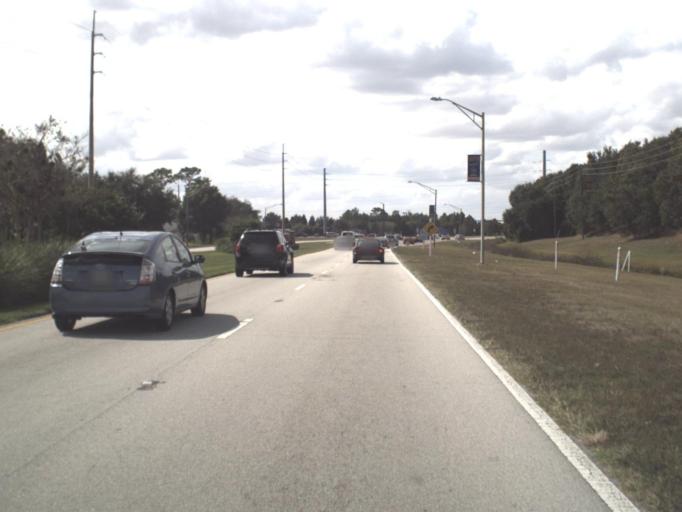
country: US
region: Florida
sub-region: Osceola County
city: Poinciana
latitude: 28.1448
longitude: -81.4672
